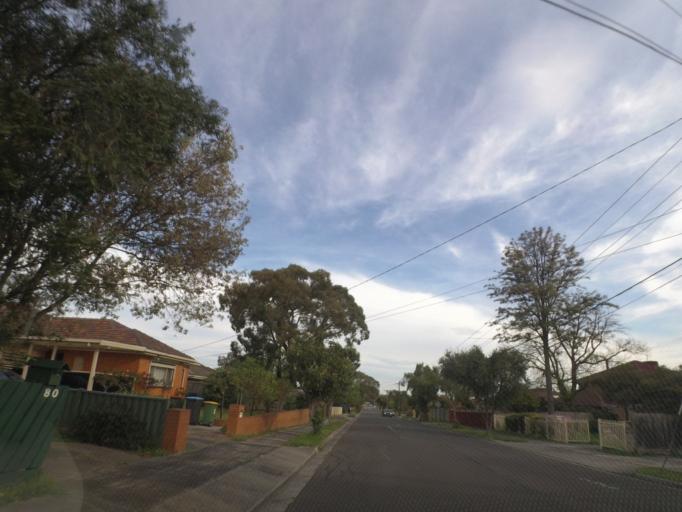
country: AU
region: Victoria
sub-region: Knox
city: Knoxfield
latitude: -37.8910
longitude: 145.2405
